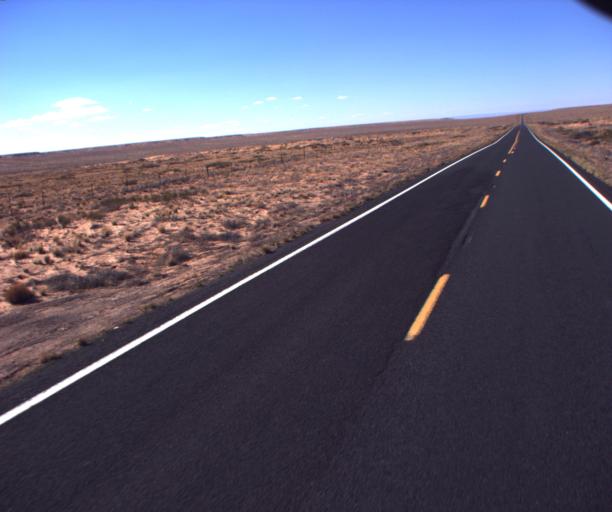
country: US
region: Arizona
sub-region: Coconino County
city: Tuba City
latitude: 36.0241
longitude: -111.1420
